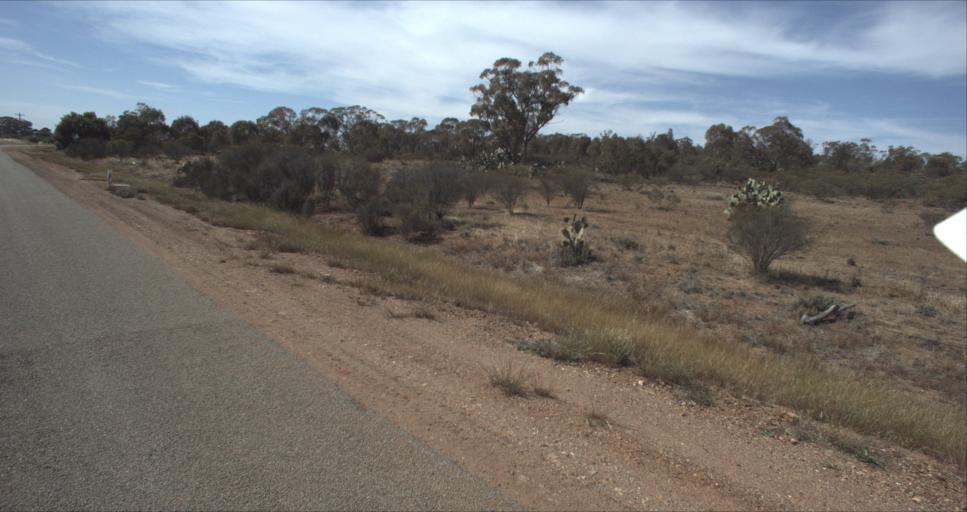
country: AU
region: New South Wales
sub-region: Leeton
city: Leeton
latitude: -34.5774
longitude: 146.4831
